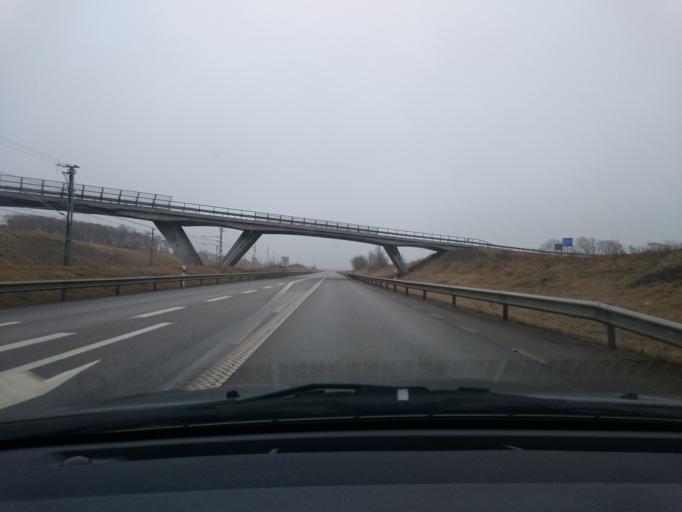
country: SE
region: Skane
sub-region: Bastads Kommun
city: Forslov
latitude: 56.3445
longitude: 12.8010
